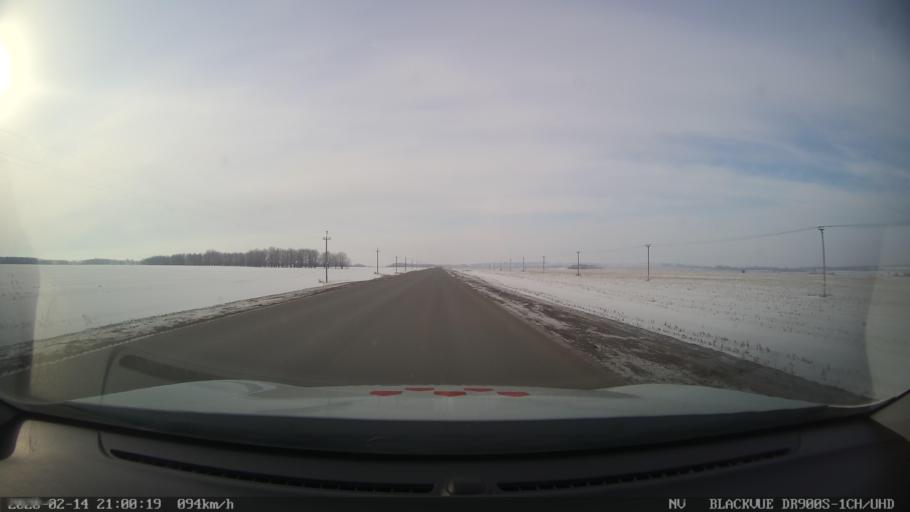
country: RU
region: Tatarstan
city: Kuybyshevskiy Zaton
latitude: 55.1720
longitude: 49.2224
